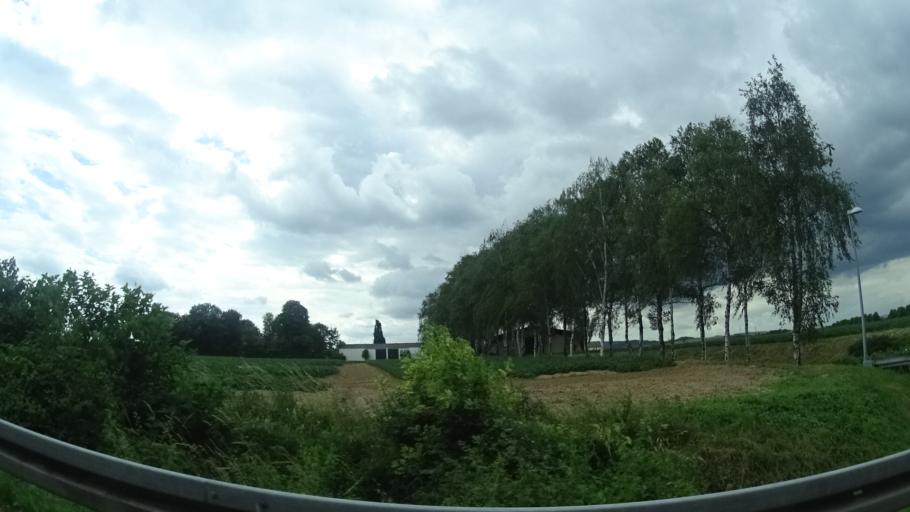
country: DE
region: Lower Saxony
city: Nordstemmen
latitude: 52.1458
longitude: 9.7618
